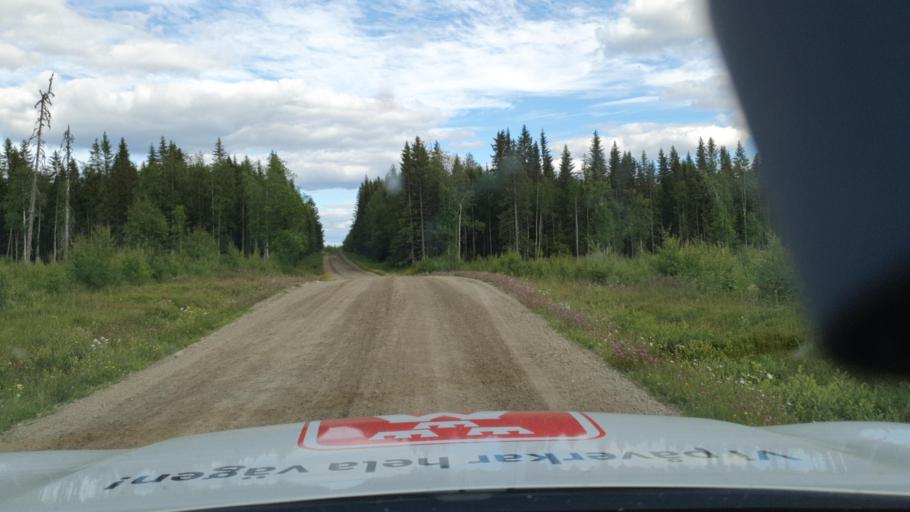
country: SE
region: Vaesterbotten
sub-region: Lycksele Kommun
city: Lycksele
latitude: 64.3446
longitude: 18.4741
